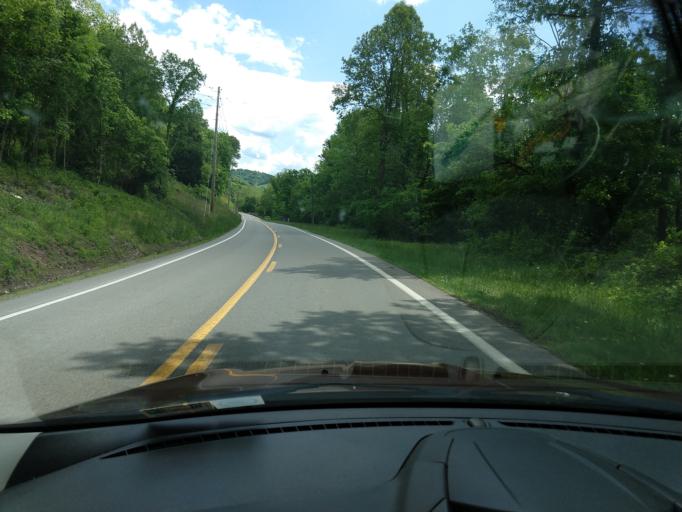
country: US
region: West Virginia
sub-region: Gilmer County
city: Glenville
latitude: 38.8807
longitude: -80.7210
